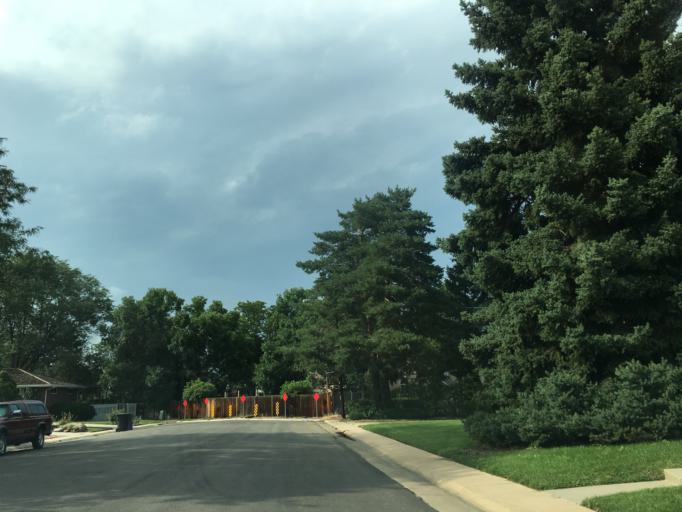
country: US
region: Colorado
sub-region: Jefferson County
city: Lakewood
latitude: 39.6783
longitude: -105.0620
